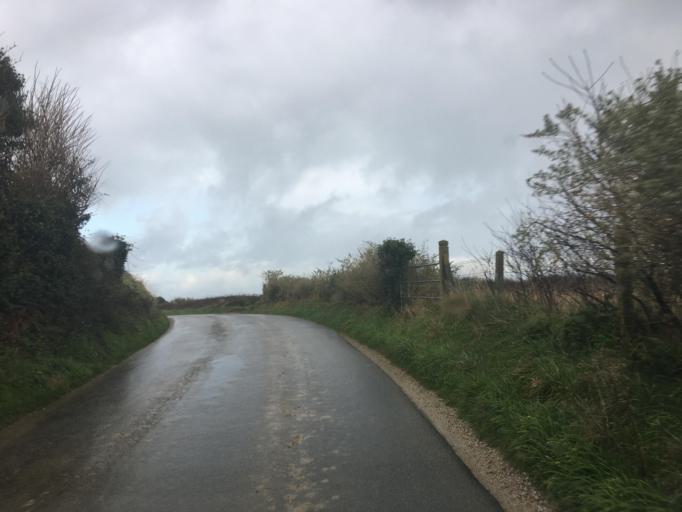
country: FR
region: Lower Normandy
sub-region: Departement de la Manche
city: Reville
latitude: 49.6908
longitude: -1.2778
